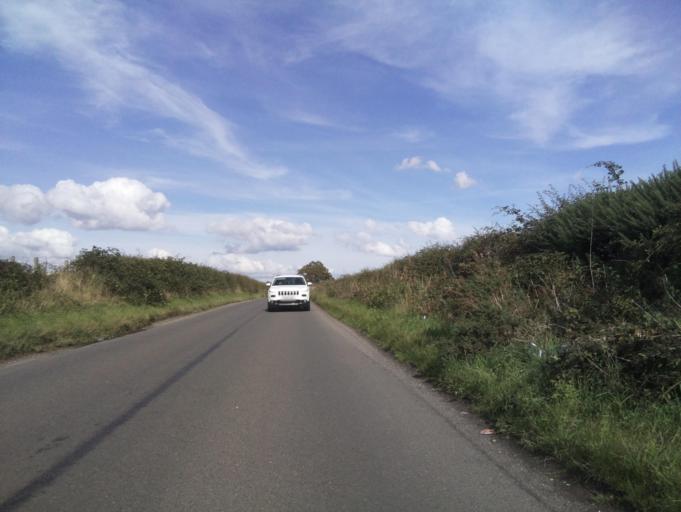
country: GB
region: Scotland
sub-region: Falkirk
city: Larbert
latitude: 56.0098
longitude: -3.8403
